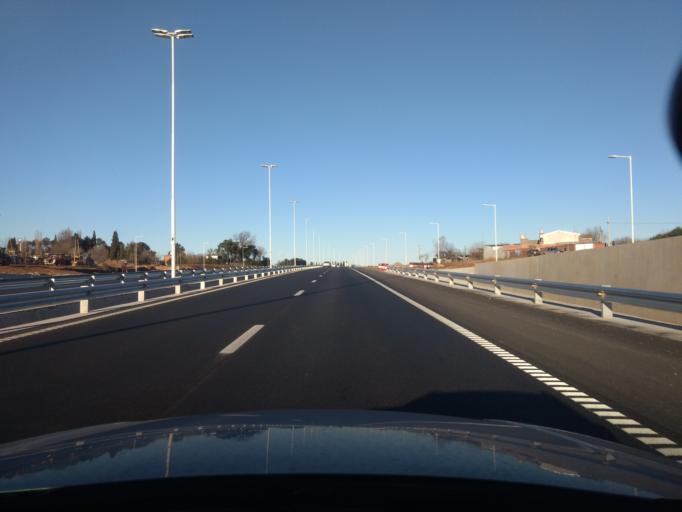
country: AR
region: Buenos Aires
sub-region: Partido de Lujan
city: Lujan
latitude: -34.5816
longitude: -59.0876
